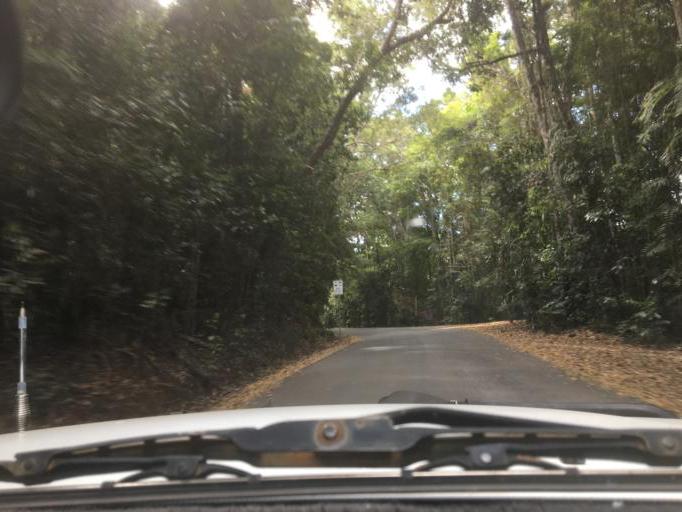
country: AU
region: Queensland
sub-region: Tablelands
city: Tolga
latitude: -17.2844
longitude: 145.6295
